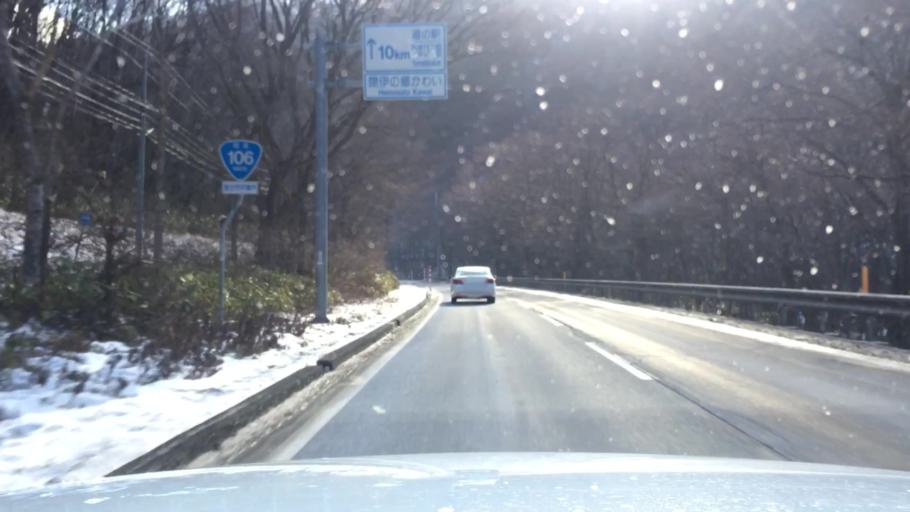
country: JP
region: Iwate
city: Tono
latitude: 39.6178
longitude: 141.4974
